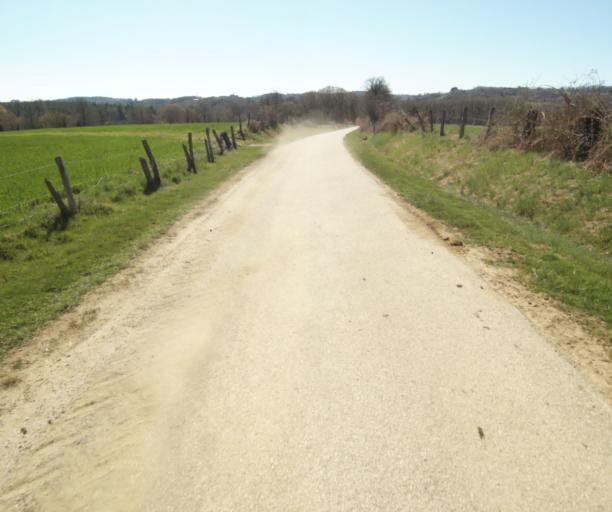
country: FR
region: Limousin
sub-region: Departement de la Correze
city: Chamboulive
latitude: 45.4247
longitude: 1.7218
